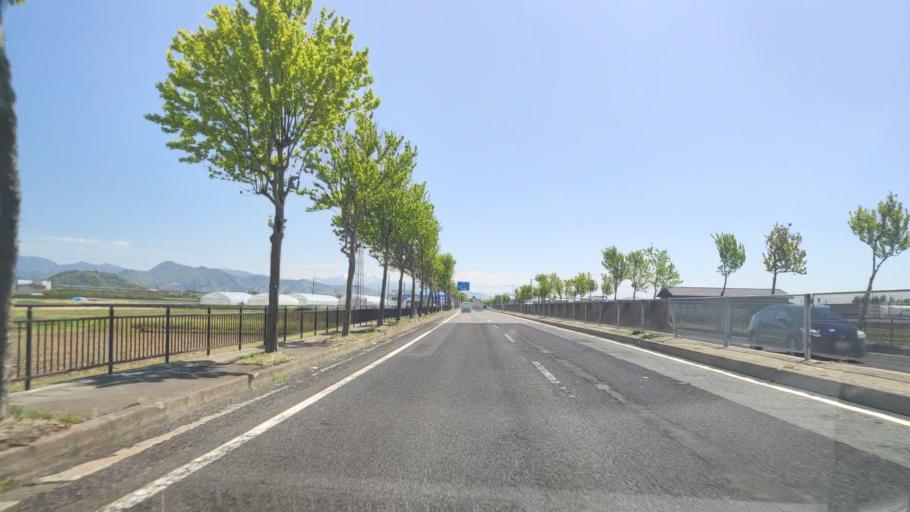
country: JP
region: Yamagata
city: Higashine
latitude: 38.4609
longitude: 140.3825
